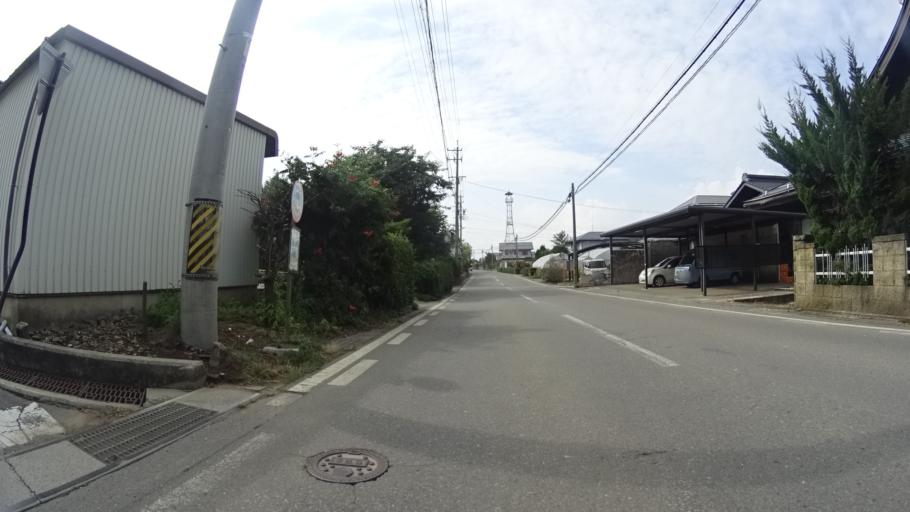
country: JP
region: Nagano
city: Chino
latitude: 35.9522
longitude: 138.2386
